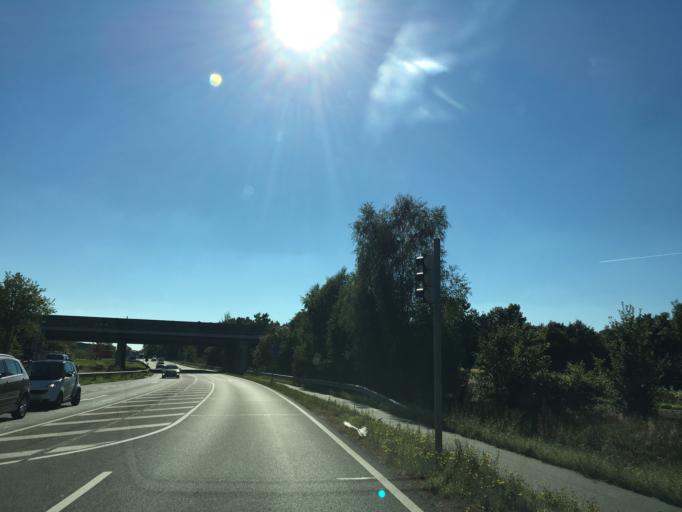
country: DE
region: Lower Saxony
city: Winsen
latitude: 53.3390
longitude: 10.2146
